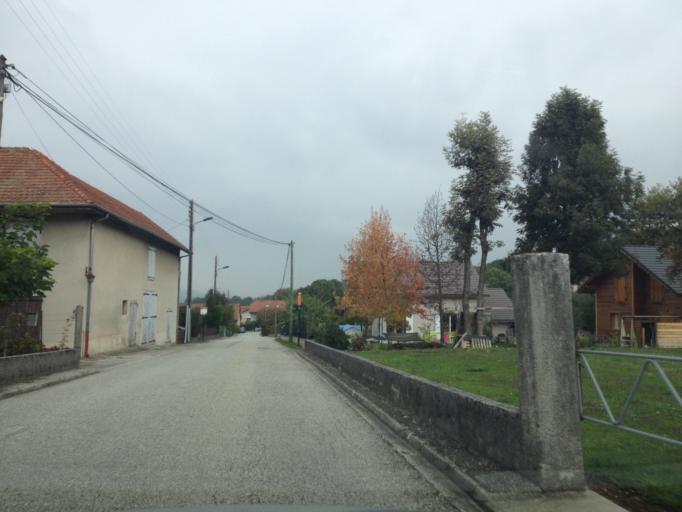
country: FR
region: Rhone-Alpes
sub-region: Departement de la Savoie
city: Mouxy
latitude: 45.6968
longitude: 5.9332
